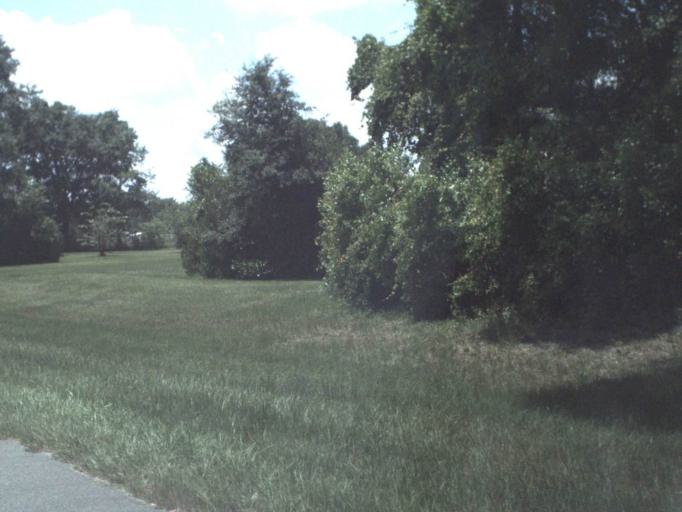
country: US
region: Florida
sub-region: Alachua County
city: High Springs
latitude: 29.7504
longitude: -82.6074
